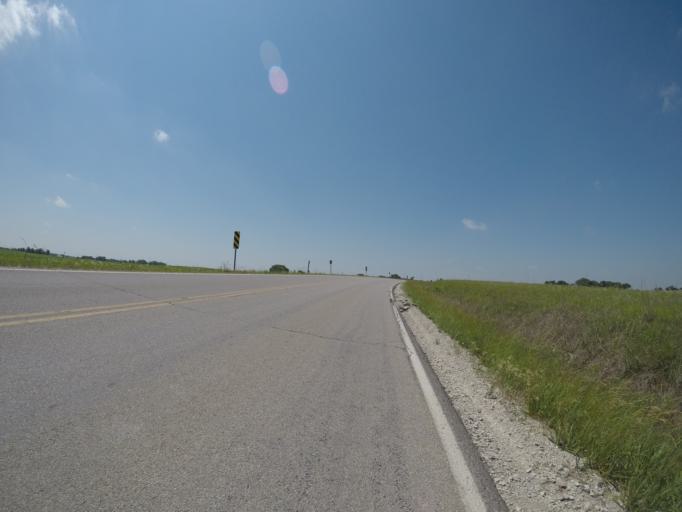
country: US
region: Kansas
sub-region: Pottawatomie County
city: Westmoreland
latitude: 39.3080
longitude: -96.4364
